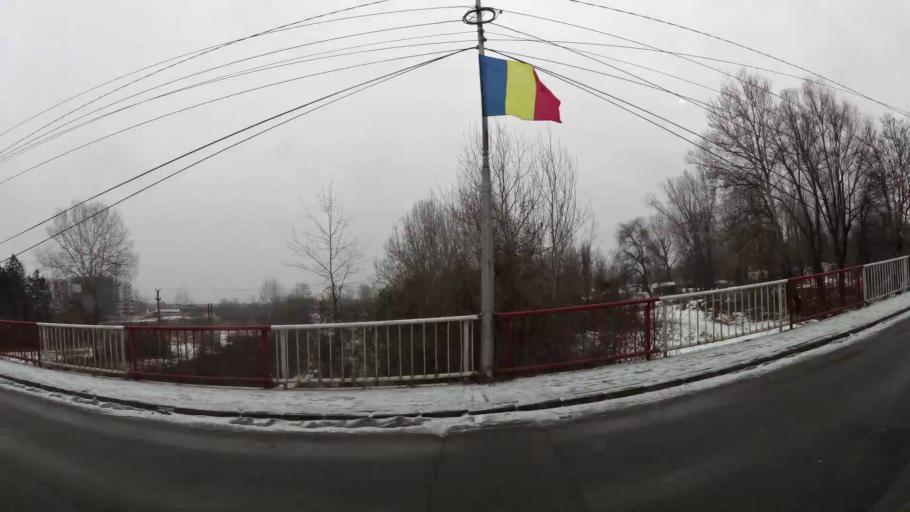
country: RO
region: Dambovita
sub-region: Municipiul Targoviste
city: Targoviste
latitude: 44.9380
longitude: 25.4563
